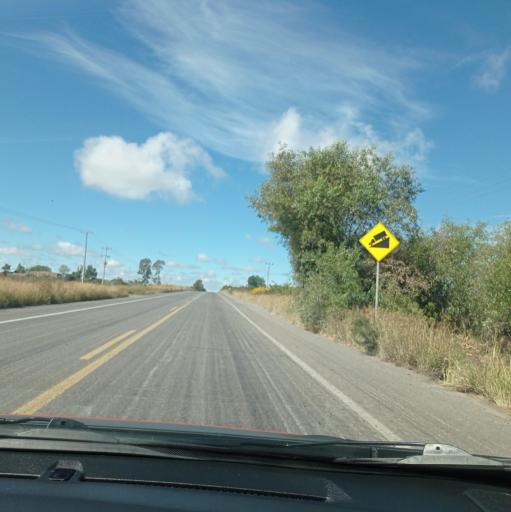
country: MX
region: Jalisco
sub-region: San Julian
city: Colonia Veintitres de Mayo
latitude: 21.0092
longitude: -102.2482
